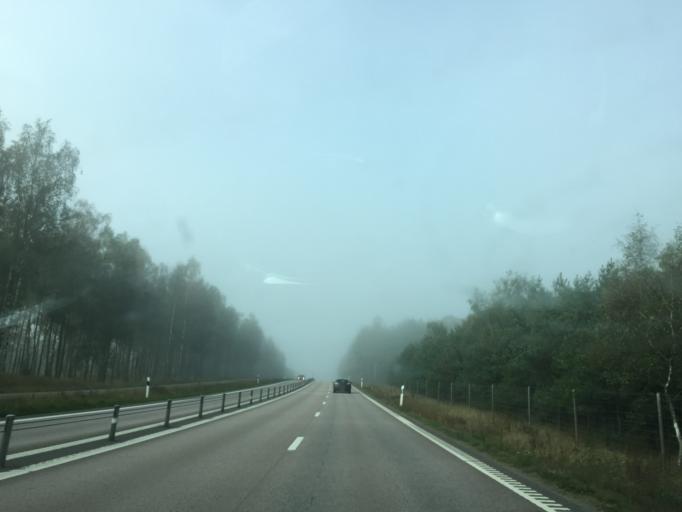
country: SE
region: Skane
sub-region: Sjobo Kommun
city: Blentarp
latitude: 55.6405
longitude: 13.5917
